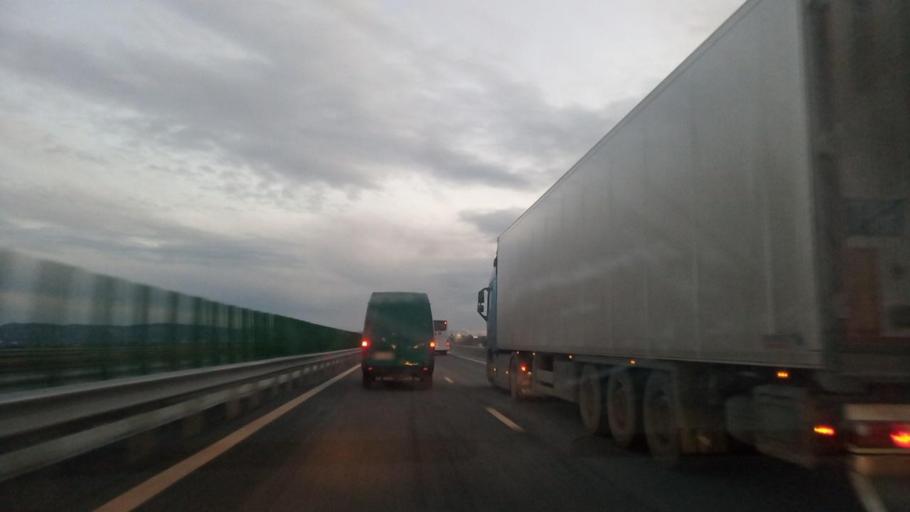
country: RO
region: Bacau
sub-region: Comuna Saucesti
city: Saucesti
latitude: 46.6135
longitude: 26.9577
